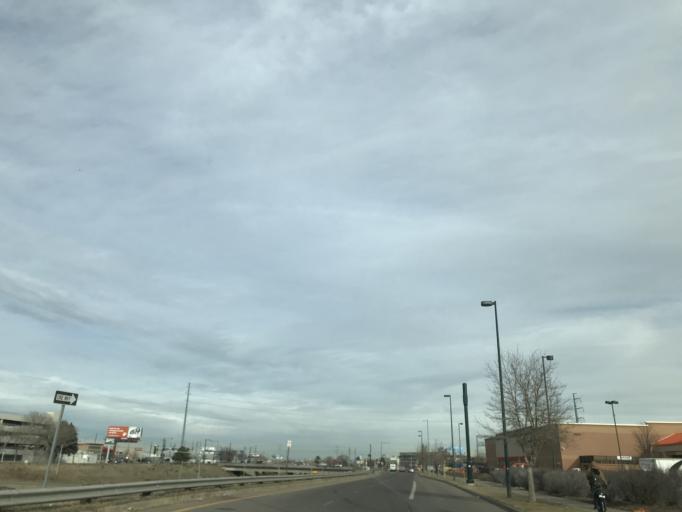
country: US
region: Colorado
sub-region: Adams County
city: Commerce City
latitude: 39.7693
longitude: -104.9025
